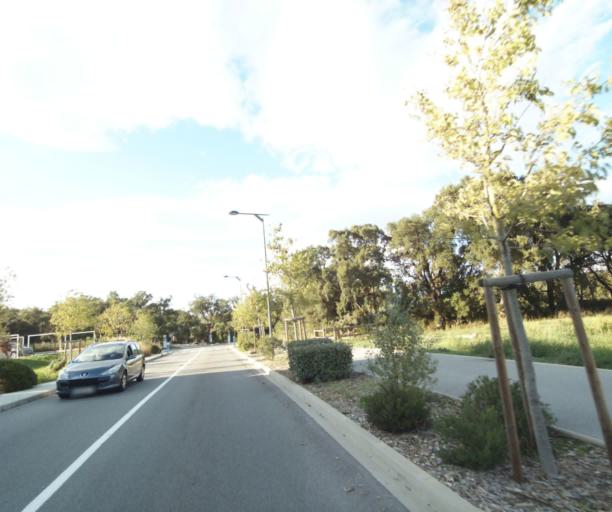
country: FR
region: Languedoc-Roussillon
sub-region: Departement des Pyrenees-Orientales
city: Argelers
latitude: 42.5570
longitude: 3.0238
